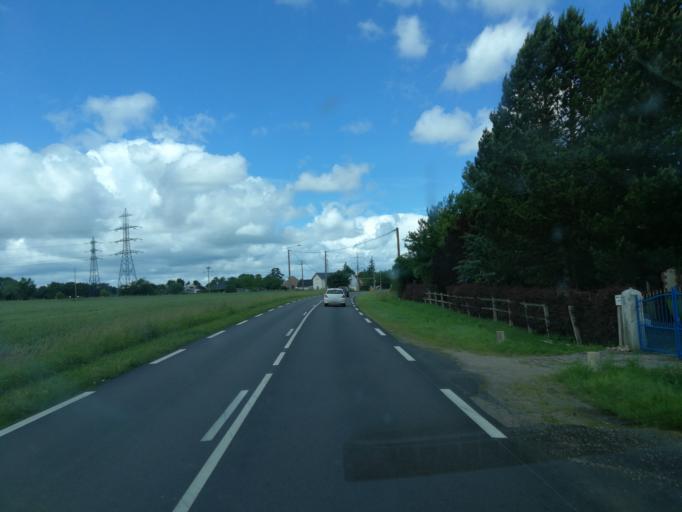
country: FR
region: Haute-Normandie
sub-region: Departement de la Seine-Maritime
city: Sahurs
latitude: 49.3513
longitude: 0.9187
